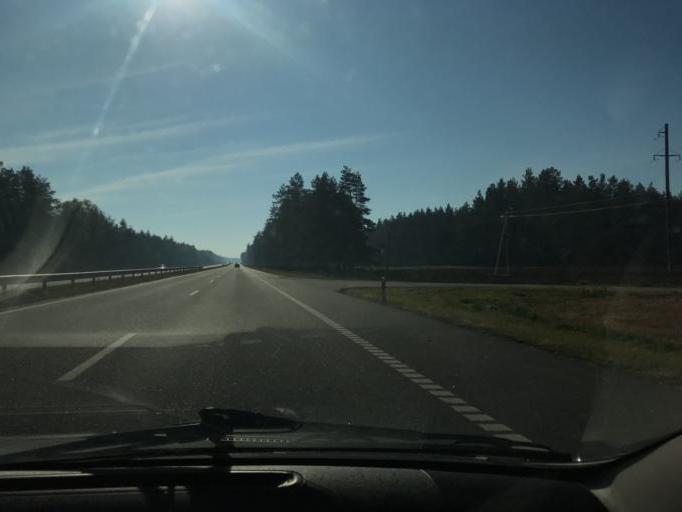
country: BY
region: Minsk
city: Slutsk
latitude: 53.3139
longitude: 27.5376
